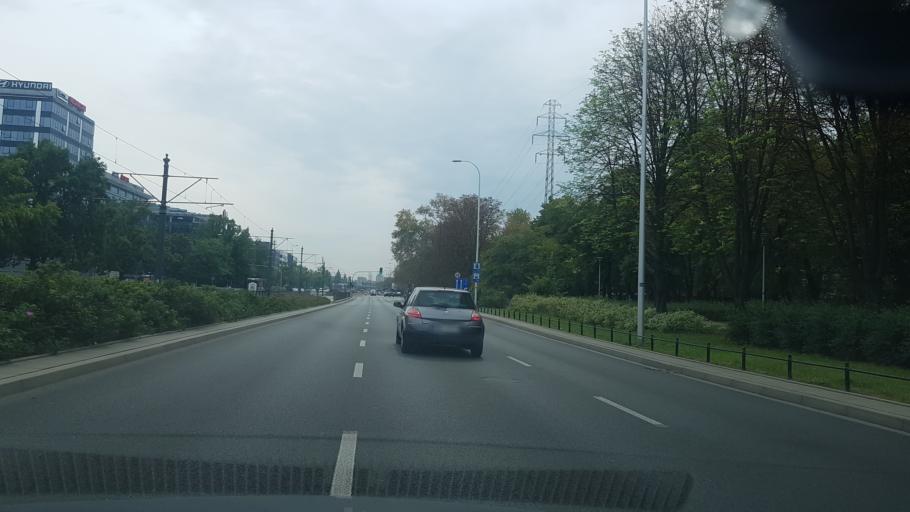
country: PL
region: Masovian Voivodeship
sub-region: Warszawa
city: Mokotow
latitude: 52.1874
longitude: 21.0020
